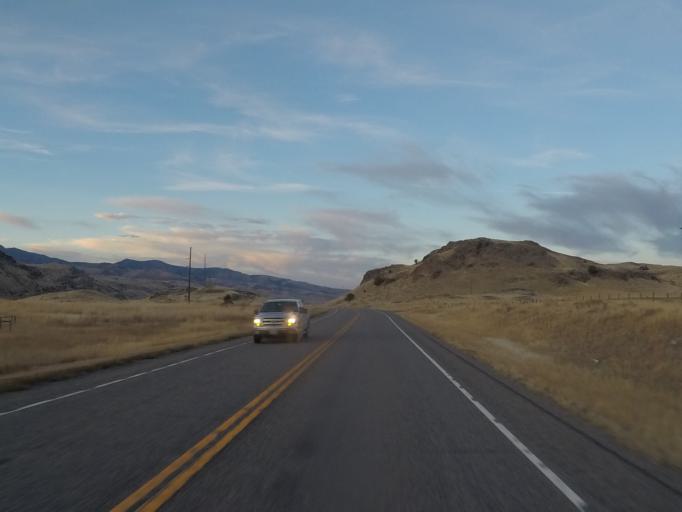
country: US
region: Montana
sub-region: Gallatin County
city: Bozeman
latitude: 45.2381
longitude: -110.8712
